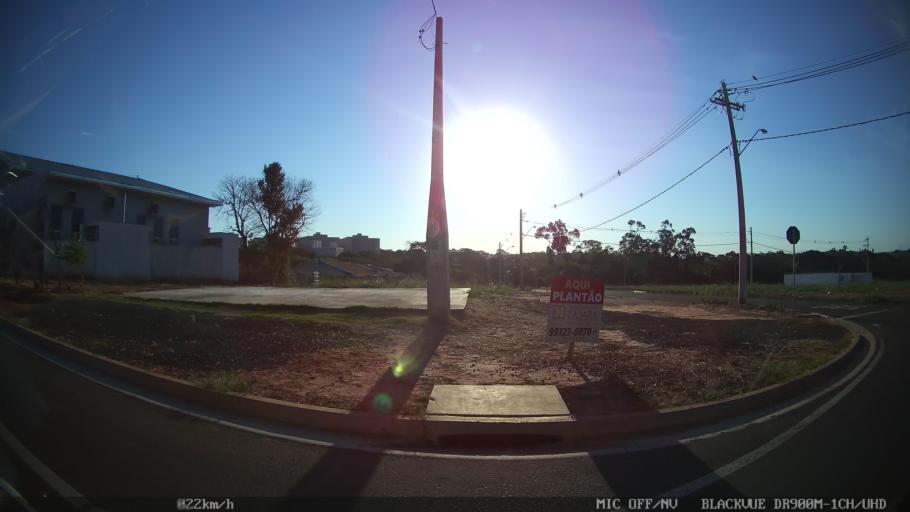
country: BR
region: Sao Paulo
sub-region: Sao Jose Do Rio Preto
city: Sao Jose do Rio Preto
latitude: -20.7872
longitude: -49.3461
